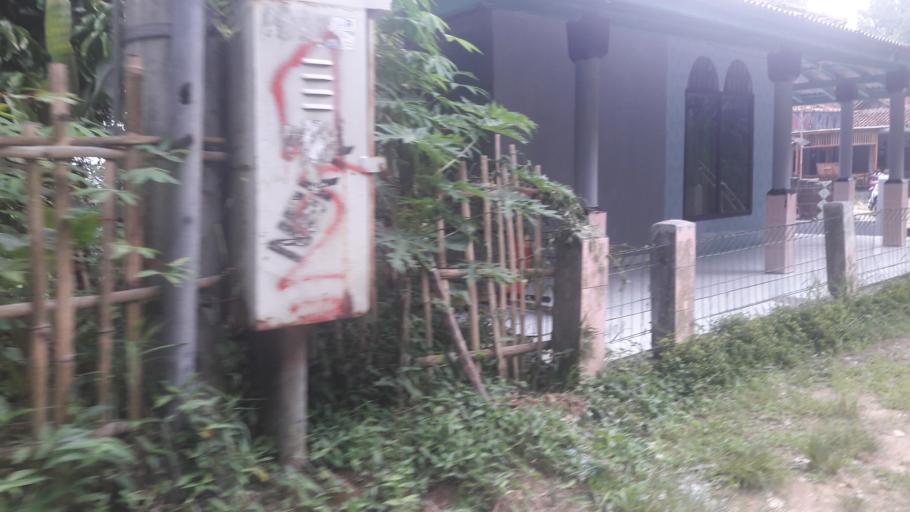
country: ID
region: West Java
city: Cipeundeuy
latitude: -6.6666
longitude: 106.5350
